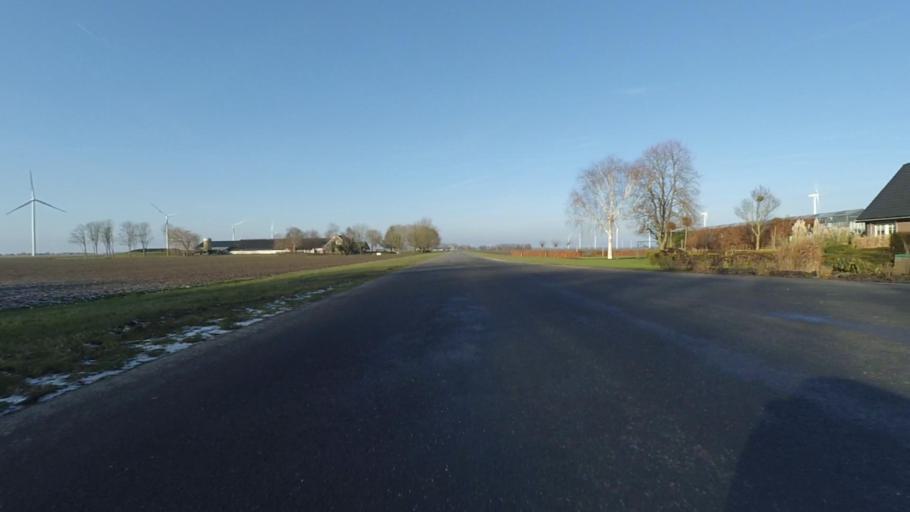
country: NL
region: Utrecht
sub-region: Gemeente Bunschoten
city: Bunschoten
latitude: 52.2863
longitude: 5.4009
